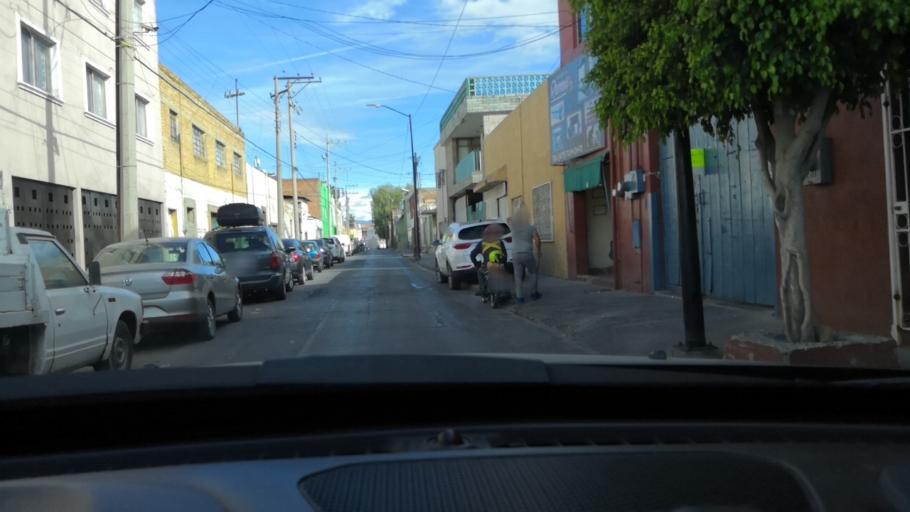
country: MX
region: Guanajuato
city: Leon
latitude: 21.1338
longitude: -101.6811
